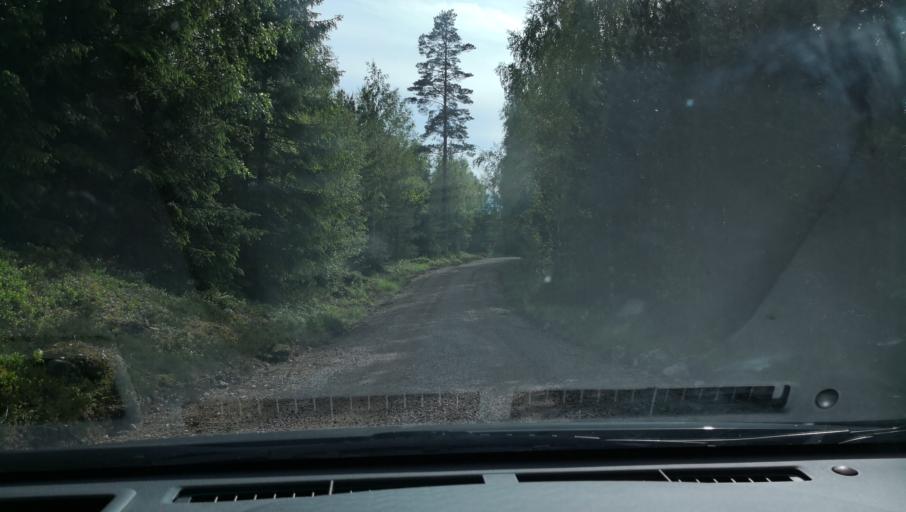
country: SE
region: Vaestmanland
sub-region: Arboga Kommun
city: Tyringe
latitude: 59.3451
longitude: 15.9265
